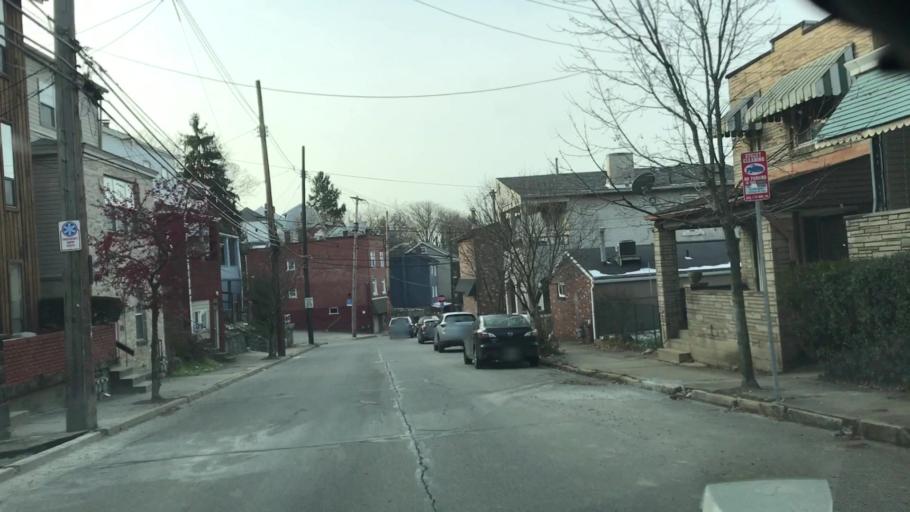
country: US
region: Pennsylvania
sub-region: Allegheny County
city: Pittsburgh
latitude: 40.4257
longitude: -80.0094
